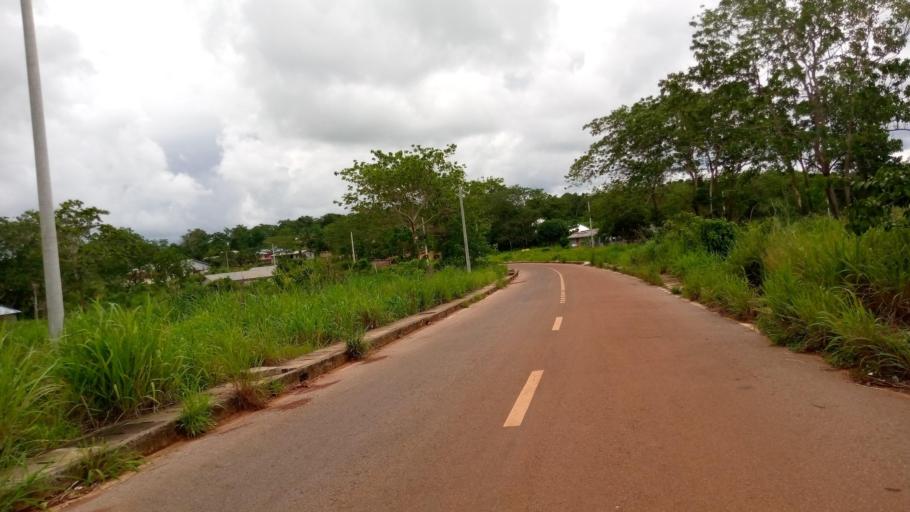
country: SL
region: Southern Province
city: Moyamba
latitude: 8.1620
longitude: -12.4502
